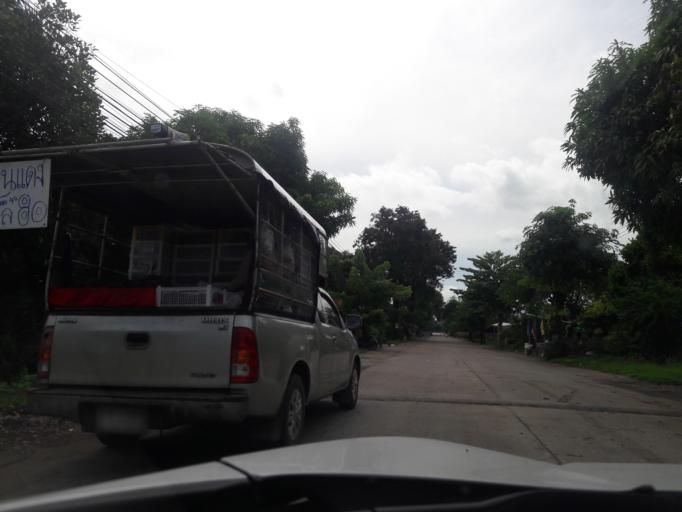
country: TH
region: Nakhon Sawan
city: Tak Fa
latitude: 15.3436
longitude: 100.4964
